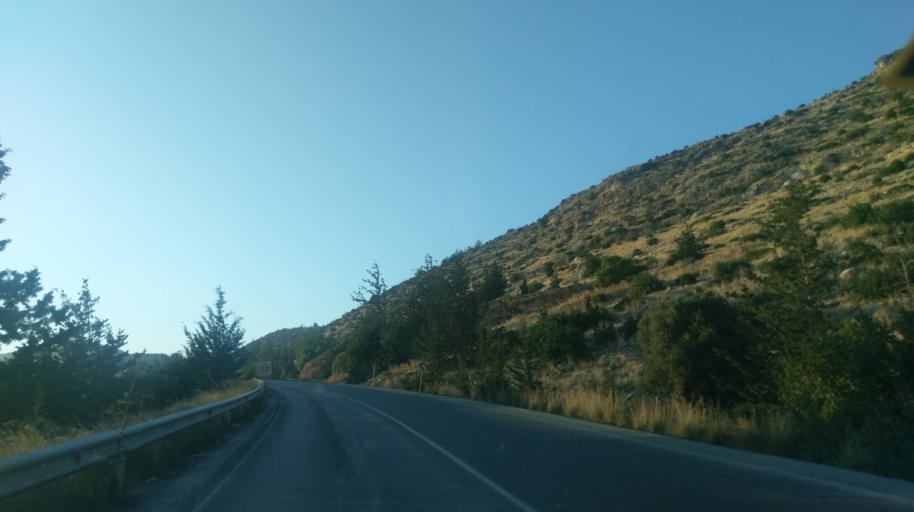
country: CY
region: Lefkosia
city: Nicosia
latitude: 35.2771
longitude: 33.4779
